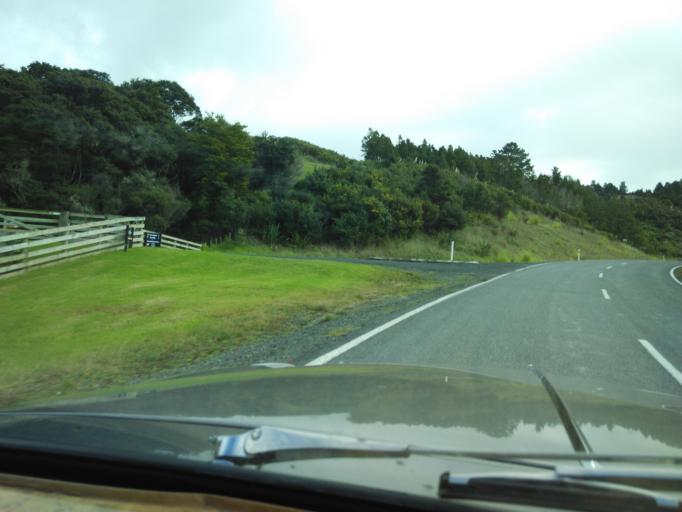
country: NZ
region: Auckland
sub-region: Auckland
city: Wellsford
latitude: -36.3363
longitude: 174.3834
